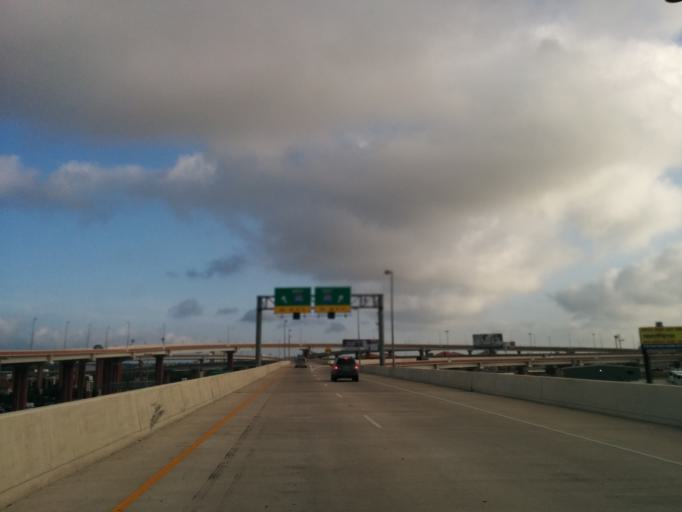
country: US
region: Texas
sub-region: Bexar County
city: Alamo Heights
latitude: 29.5164
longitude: -98.4776
